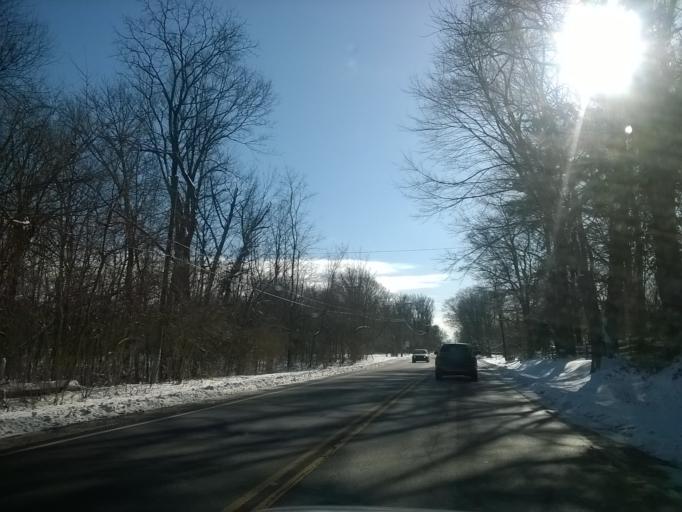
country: US
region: Indiana
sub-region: Hamilton County
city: Carmel
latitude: 39.9499
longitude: -86.1269
